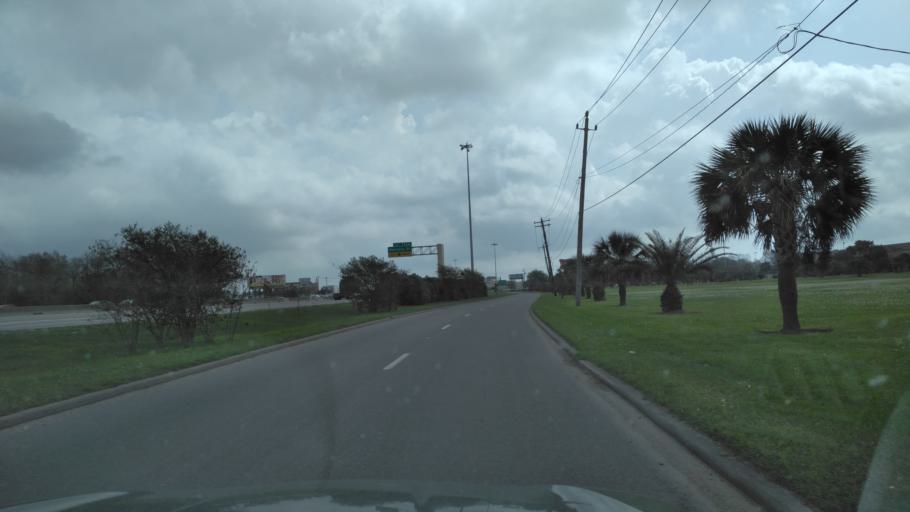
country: US
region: Texas
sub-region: Harris County
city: Jacinto City
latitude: 29.7738
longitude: -95.2550
